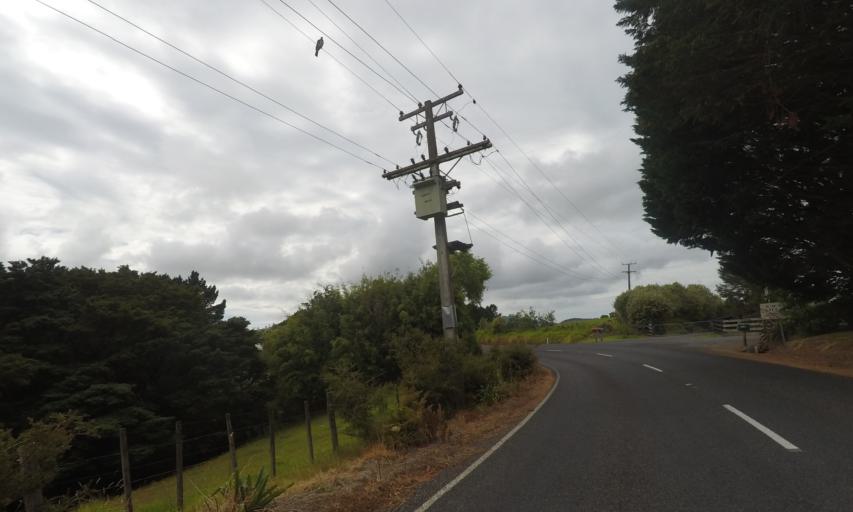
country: NZ
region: Northland
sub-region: Whangarei
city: Whangarei
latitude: -35.7608
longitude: 174.4556
